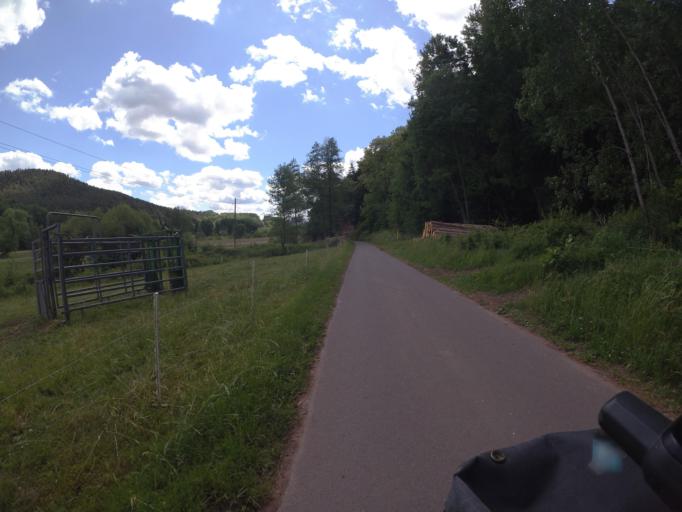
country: DE
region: Rheinland-Pfalz
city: Bruchweiler-Barenbach
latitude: 49.1264
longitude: 7.8006
